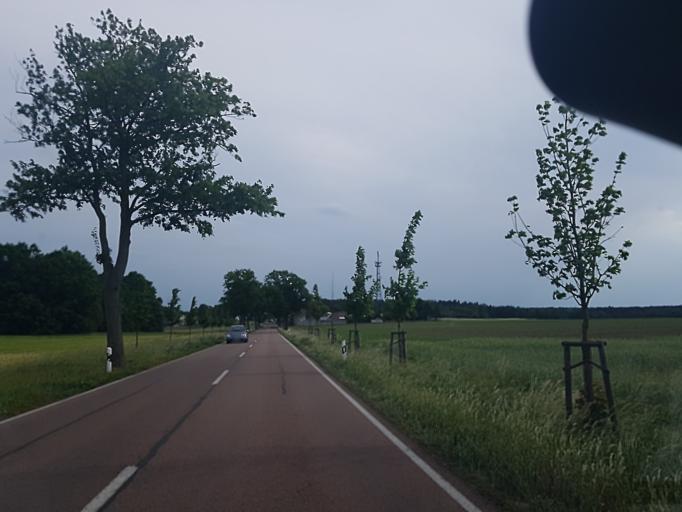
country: DE
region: Saxony-Anhalt
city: Nudersdorf
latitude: 51.9149
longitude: 12.6062
